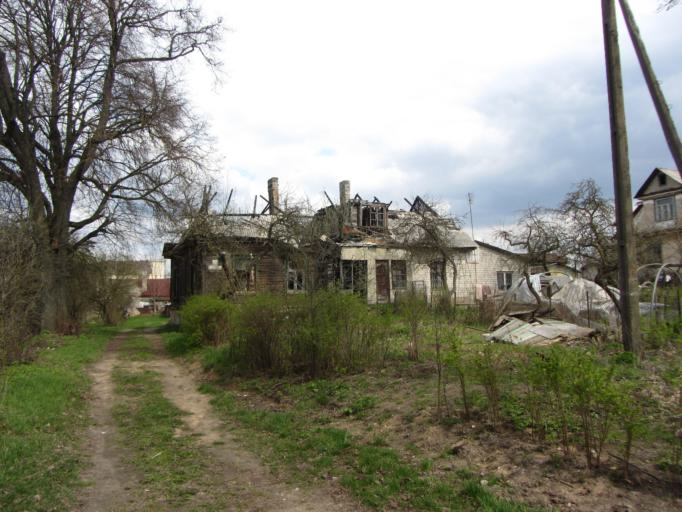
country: LT
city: Lentvaris
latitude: 54.6451
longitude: 25.0576
